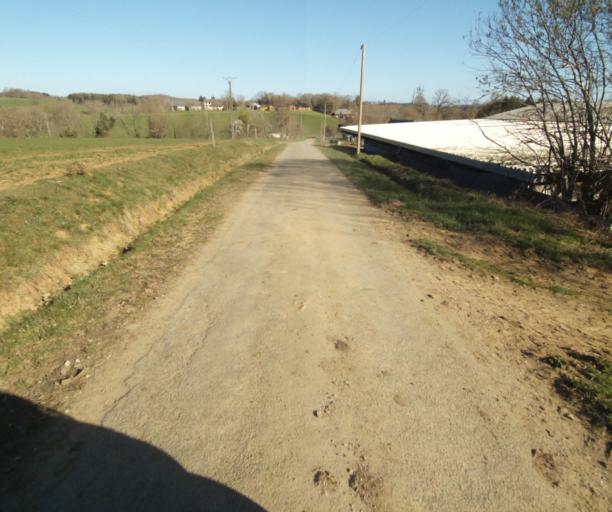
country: FR
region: Limousin
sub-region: Departement de la Correze
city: Seilhac
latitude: 45.3792
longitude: 1.7642
